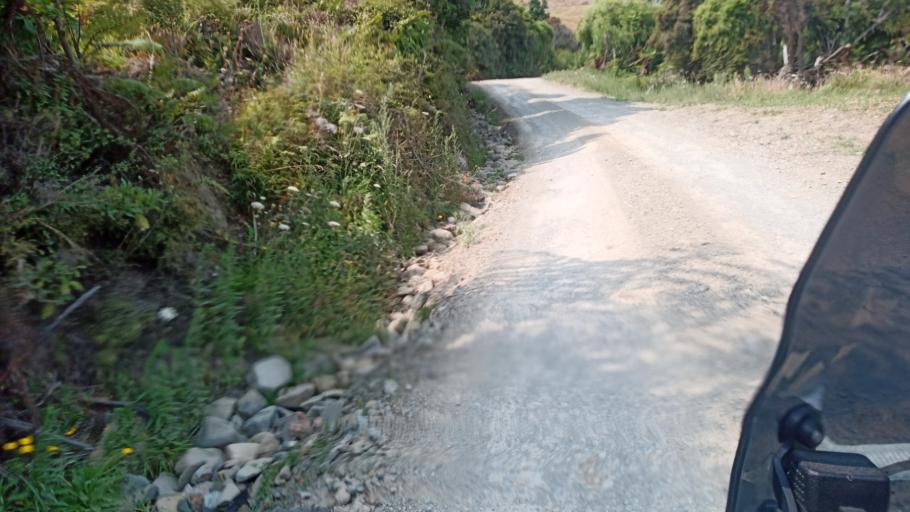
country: NZ
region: Bay of Plenty
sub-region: Opotiki District
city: Opotiki
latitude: -37.6459
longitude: 178.1376
